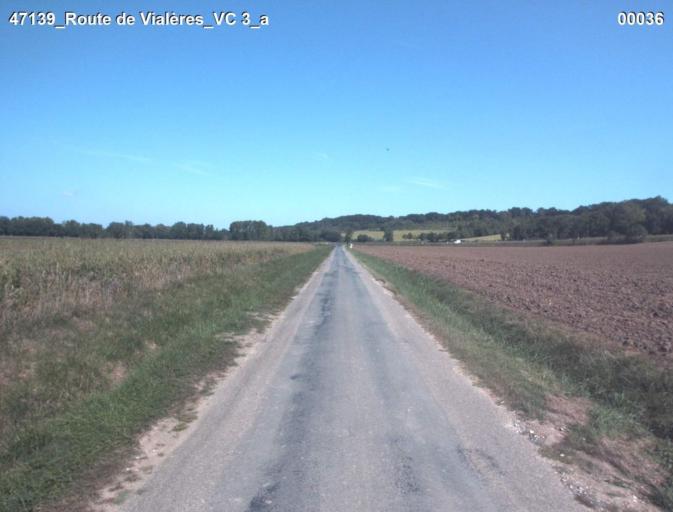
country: FR
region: Aquitaine
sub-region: Departement du Lot-et-Garonne
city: Nerac
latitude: 44.0613
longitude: 0.3850
